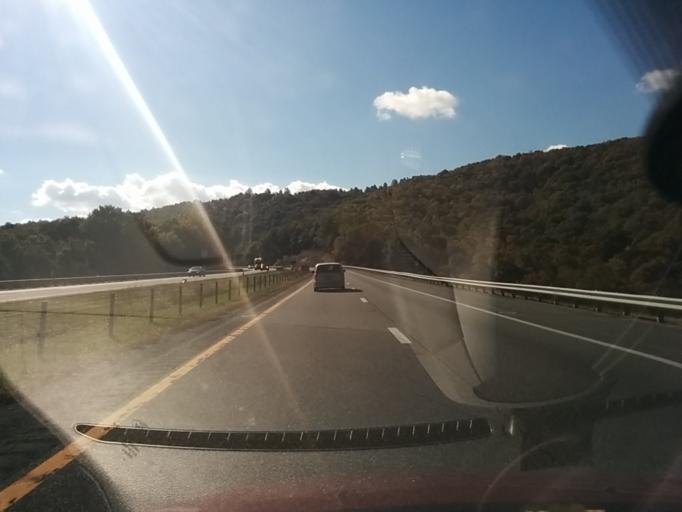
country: US
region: Virginia
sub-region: City of Waynesboro
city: Waynesboro
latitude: 38.0376
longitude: -78.8711
